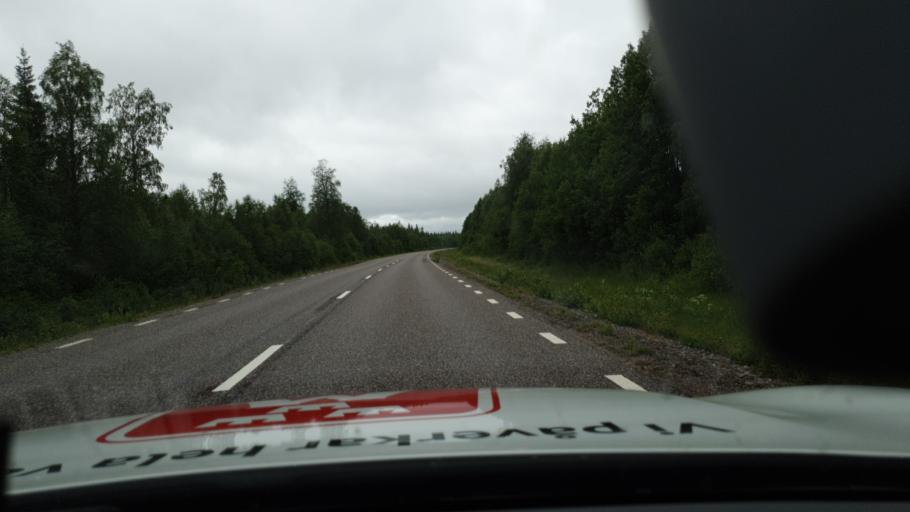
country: SE
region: Norrbotten
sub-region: Pajala Kommun
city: Pajala
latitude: 67.1156
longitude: 23.6147
